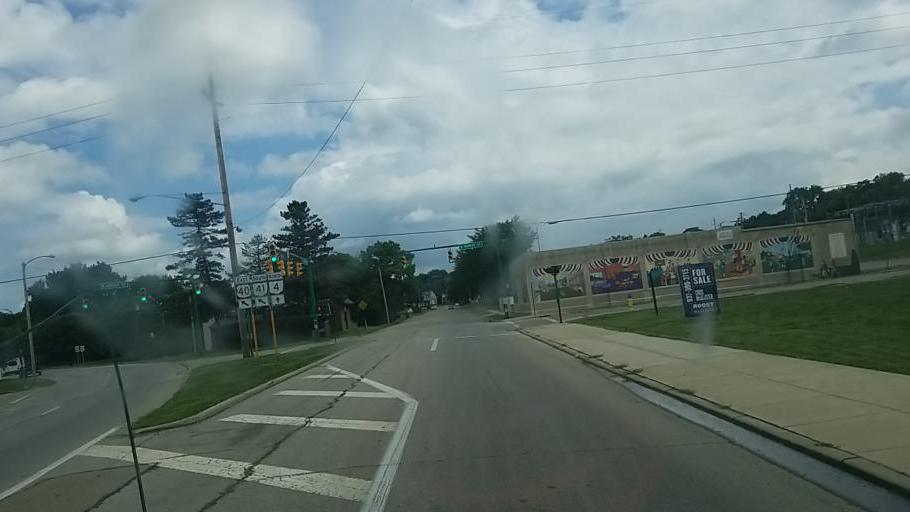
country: US
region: Ohio
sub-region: Clark County
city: Springfield
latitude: 39.9252
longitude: -83.8008
